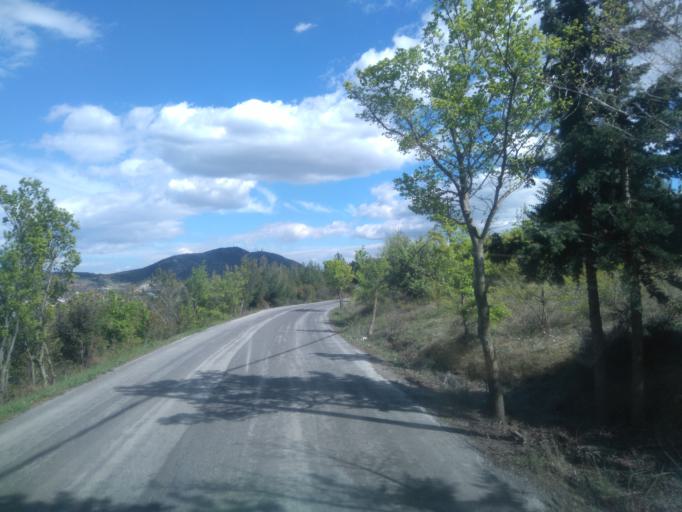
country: GR
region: Central Macedonia
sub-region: Nomos Thessalonikis
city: Pefka
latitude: 40.6420
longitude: 23.0045
